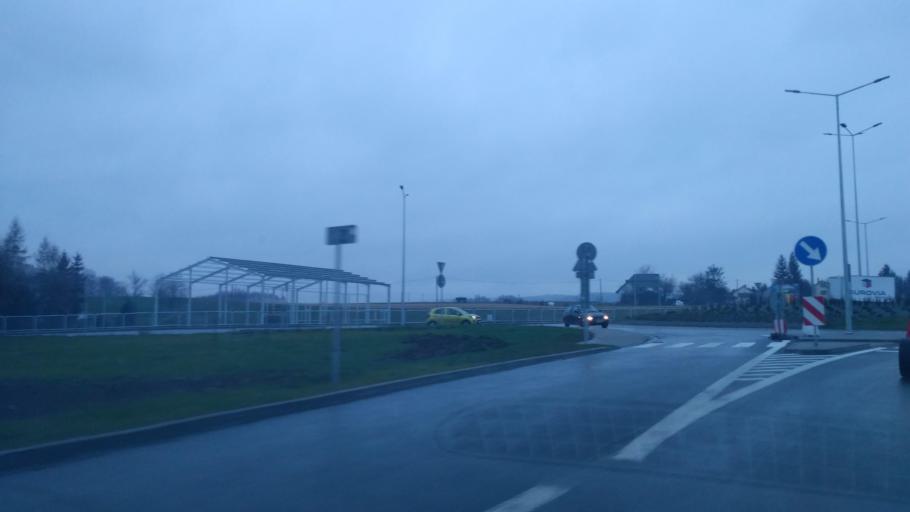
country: PL
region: Subcarpathian Voivodeship
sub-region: Powiat rzeszowski
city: Dynow
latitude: 49.8348
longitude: 22.2429
